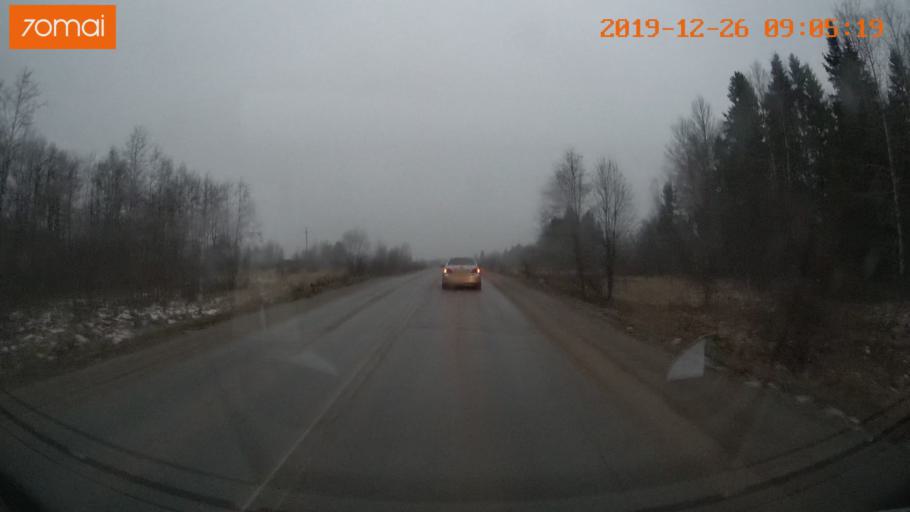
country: RU
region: Vologda
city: Gryazovets
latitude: 58.8244
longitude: 40.2585
